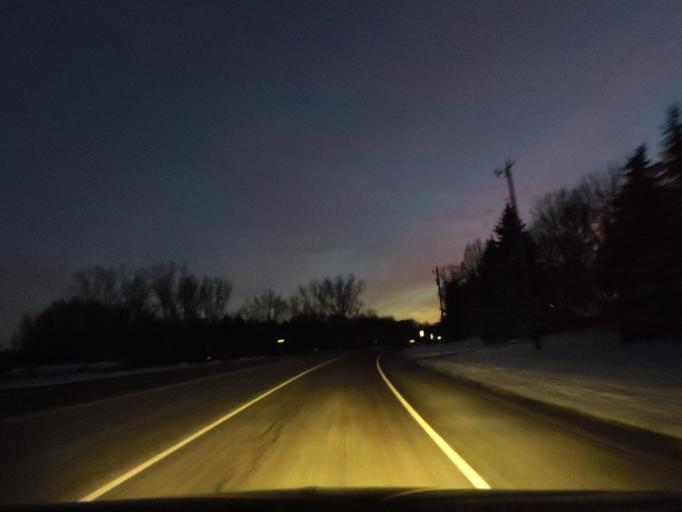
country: US
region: Minnesota
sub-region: Chisago County
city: Chisago City
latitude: 45.3367
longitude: -92.8820
